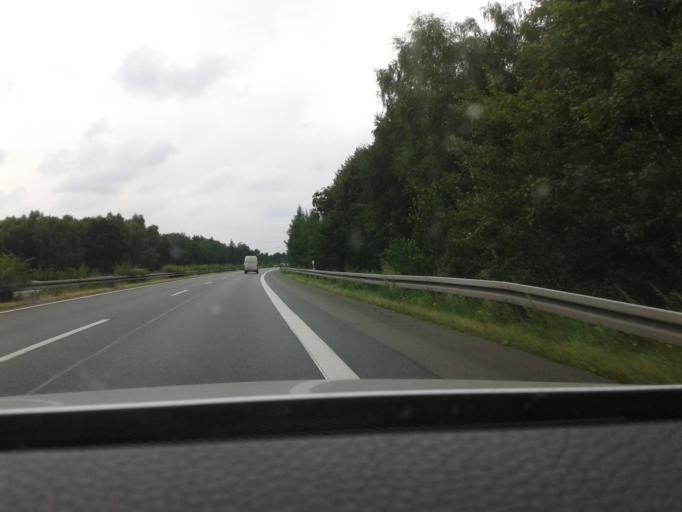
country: DE
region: Lower Saxony
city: Burgdorf
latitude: 52.4390
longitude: 9.9265
